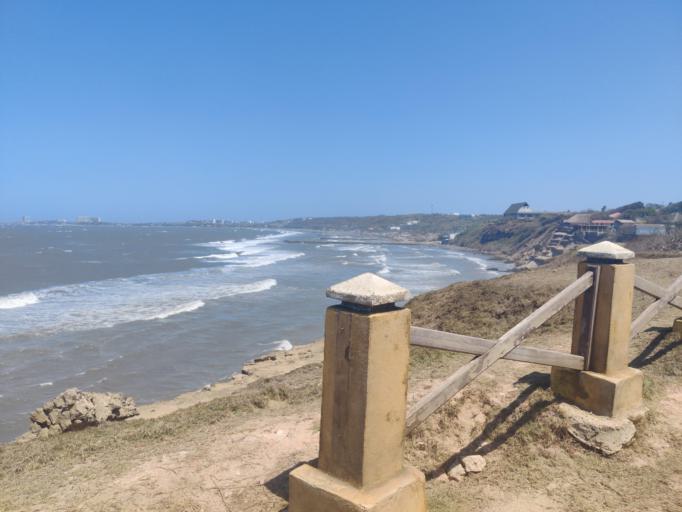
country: CO
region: Atlantico
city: Puerto Colombia
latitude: 11.0186
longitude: -74.9415
